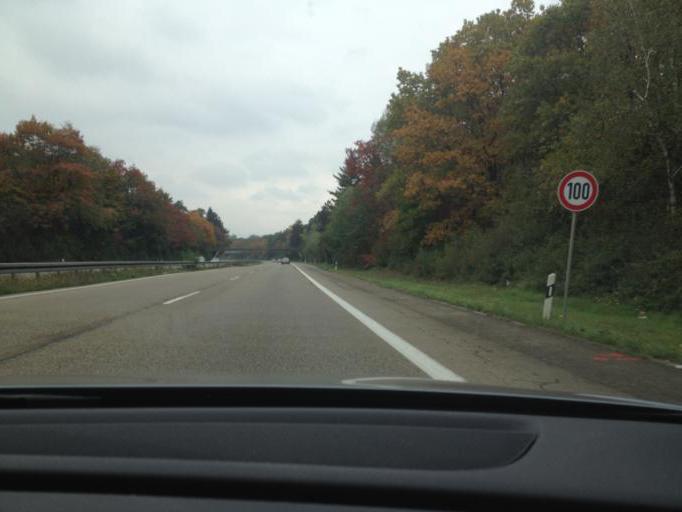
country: DE
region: Baden-Wuerttemberg
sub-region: Karlsruhe Region
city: Bruhl
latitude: 49.4291
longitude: 8.5372
